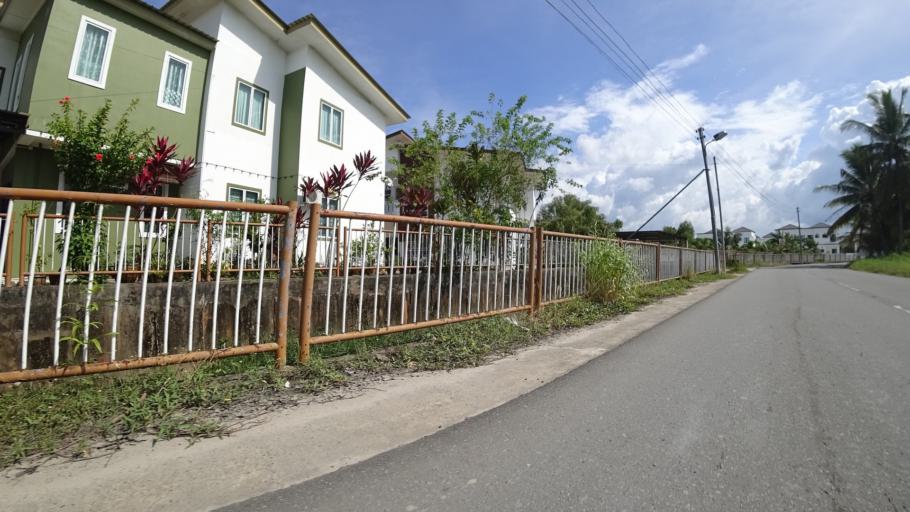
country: BN
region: Brunei and Muara
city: Bandar Seri Begawan
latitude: 4.8851
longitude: 114.8535
